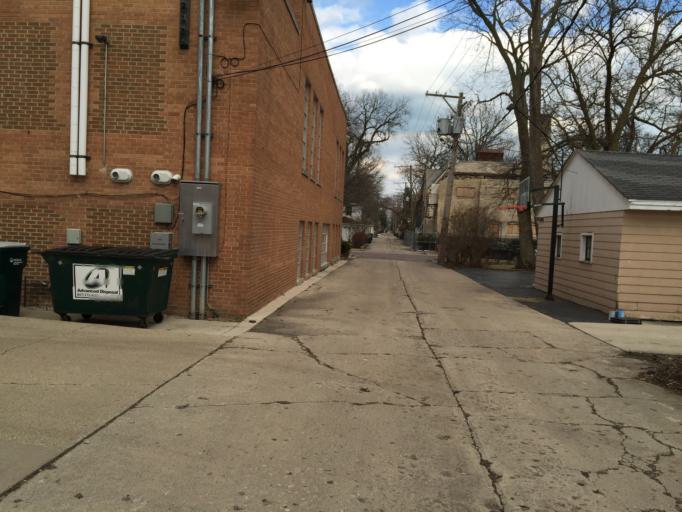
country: US
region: Illinois
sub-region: Cook County
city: Kenilworth
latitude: 42.0760
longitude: -87.7035
